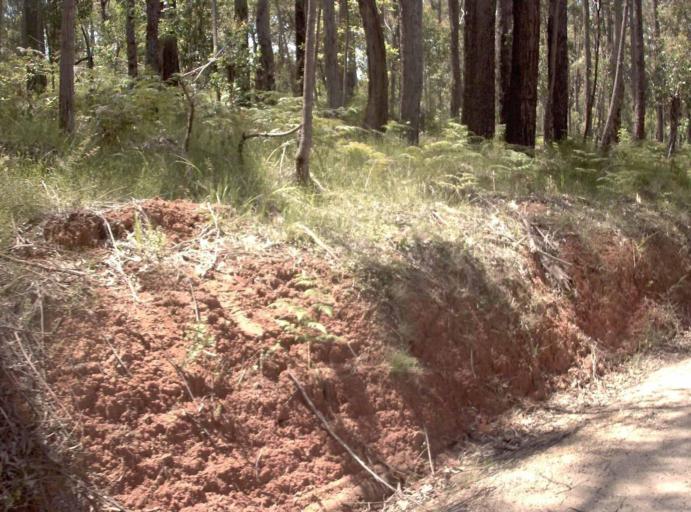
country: AU
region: New South Wales
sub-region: Bombala
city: Bombala
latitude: -37.5780
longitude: 149.0158
